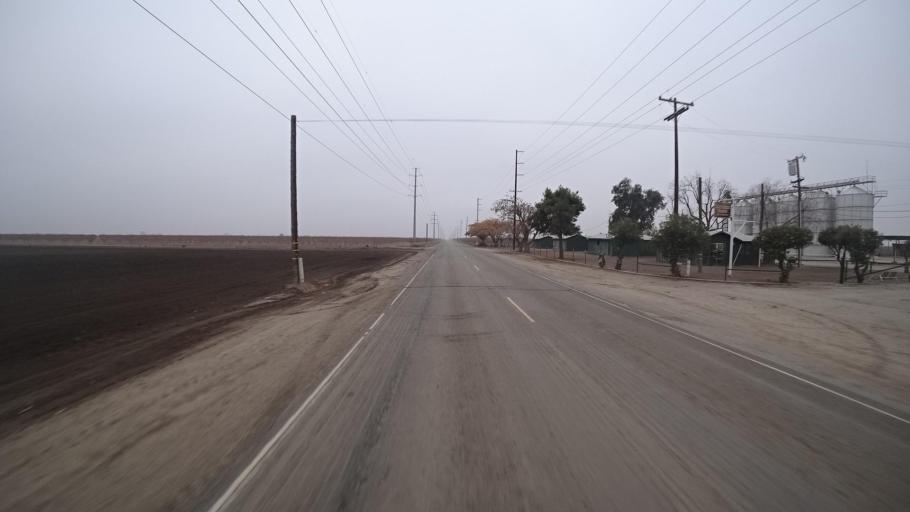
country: US
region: California
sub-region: Kern County
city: Buttonwillow
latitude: 35.3913
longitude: -119.4476
